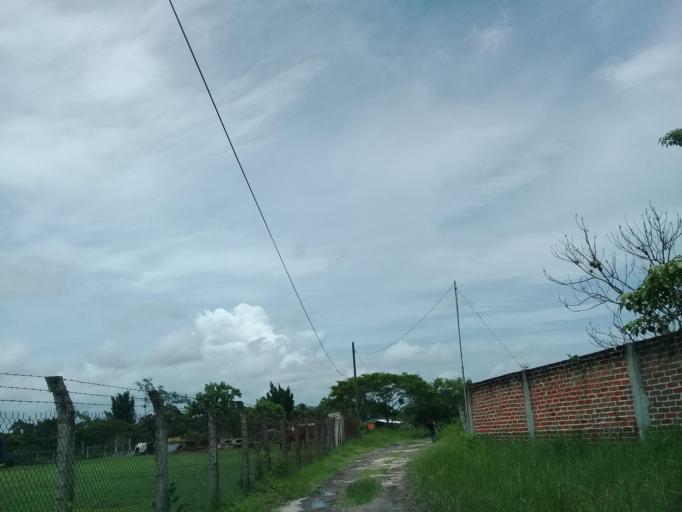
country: MX
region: Veracruz
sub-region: Emiliano Zapata
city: Dos Rios
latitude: 19.4710
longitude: -96.7808
